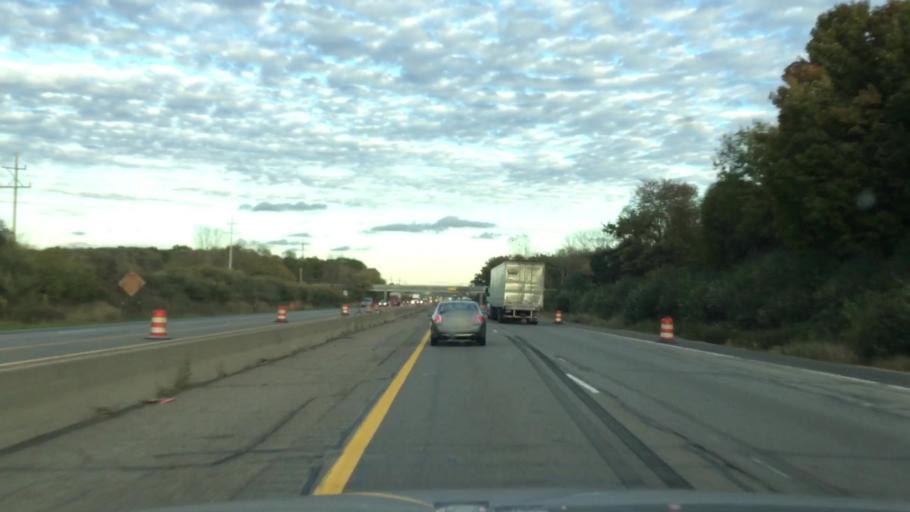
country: US
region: Michigan
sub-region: Jackson County
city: Jackson
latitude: 42.2690
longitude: -84.4867
